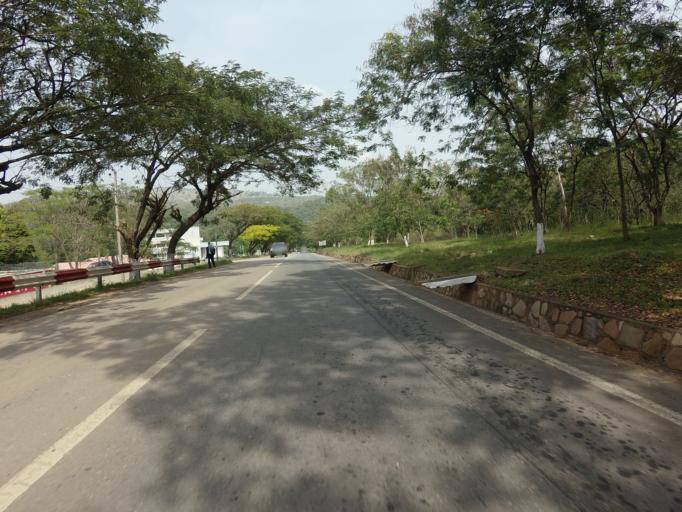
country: GH
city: Akropong
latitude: 6.2739
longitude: 0.0534
